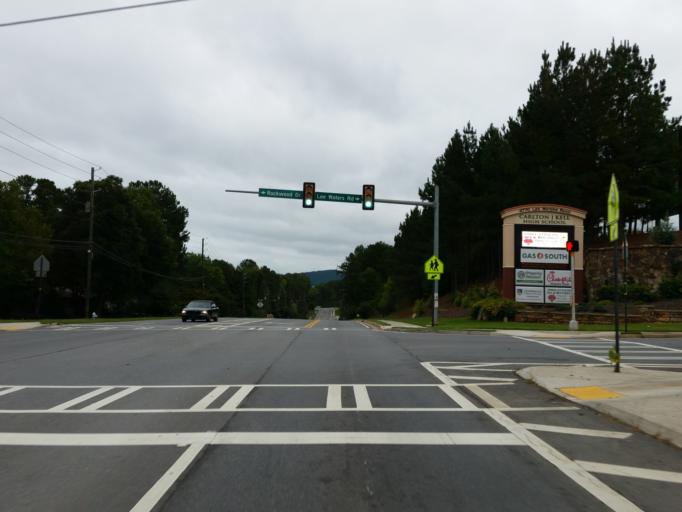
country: US
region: Georgia
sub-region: Cherokee County
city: Woodstock
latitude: 34.0679
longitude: -84.5141
